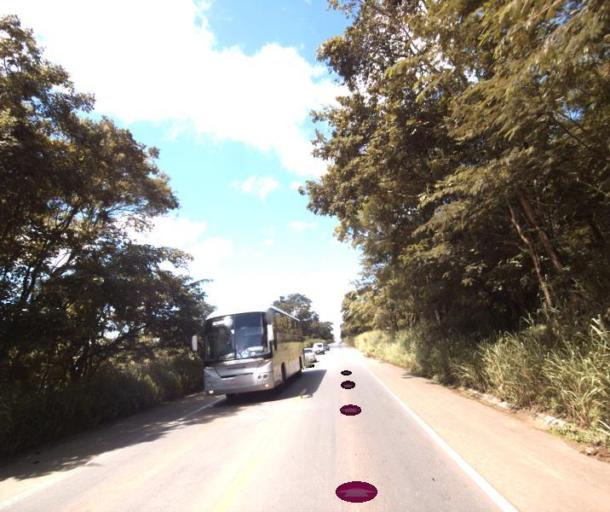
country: BR
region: Goias
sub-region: Jaragua
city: Jaragua
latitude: -15.7899
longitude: -49.3024
